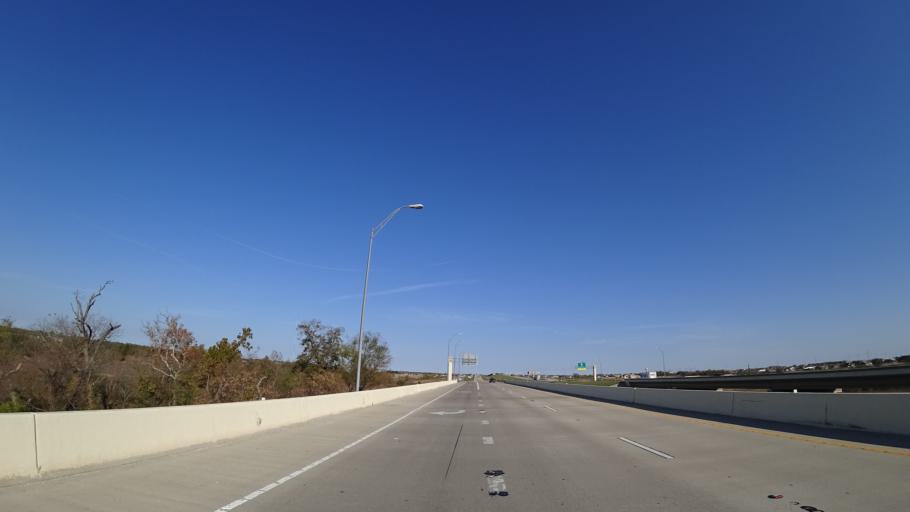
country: US
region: Texas
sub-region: Williamson County
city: Hutto
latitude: 30.5260
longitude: -97.5764
